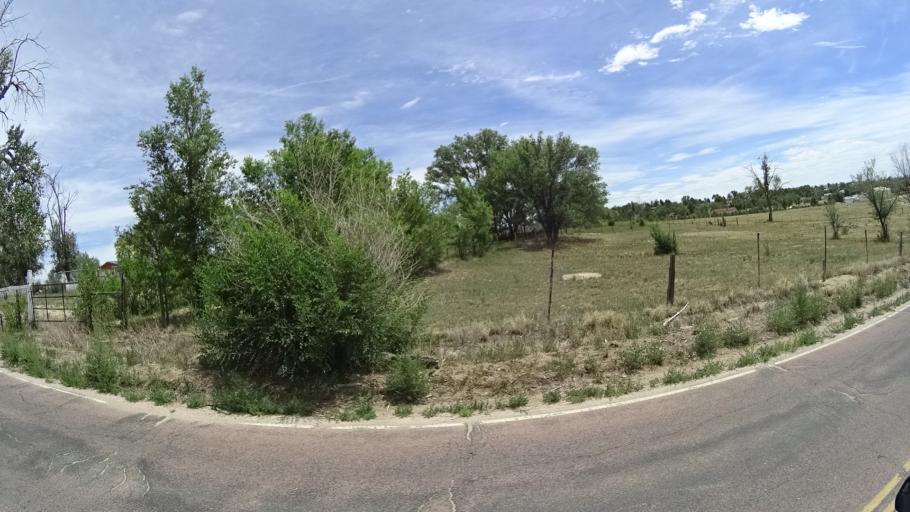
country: US
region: Colorado
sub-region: El Paso County
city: Fountain
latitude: 38.6812
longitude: -104.6736
